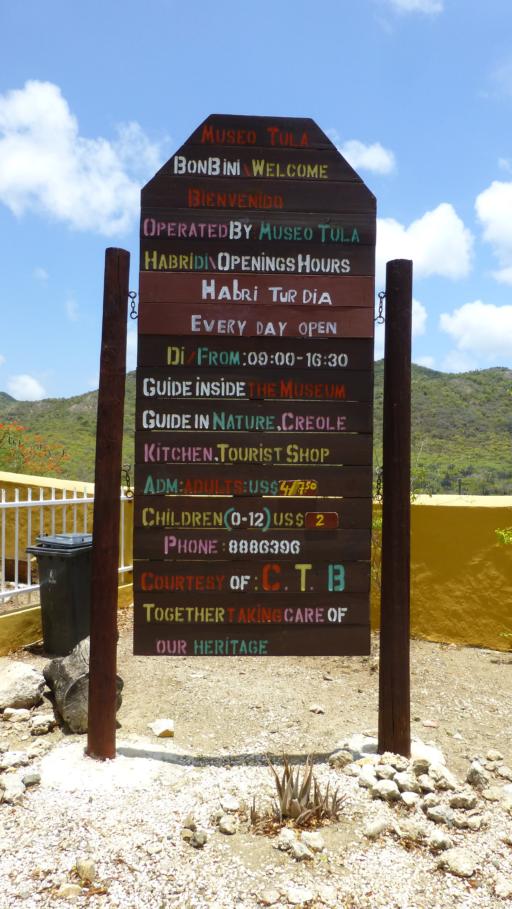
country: CW
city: Dorp Soto
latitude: 12.3446
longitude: -69.1438
